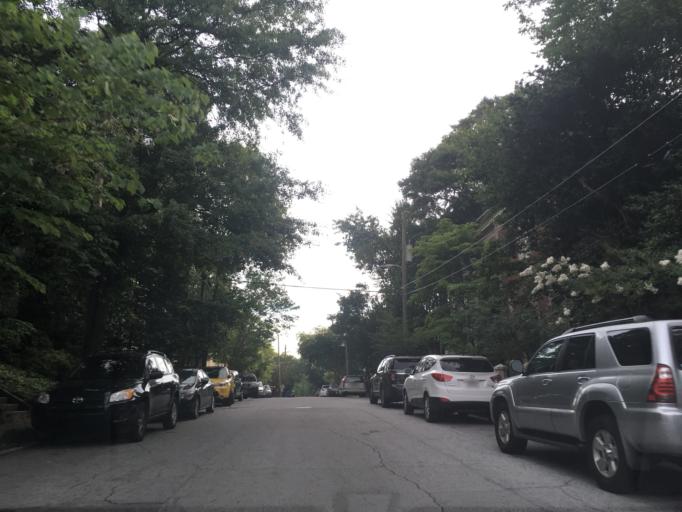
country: US
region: Georgia
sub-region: DeKalb County
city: Druid Hills
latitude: 33.7745
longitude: -84.3556
